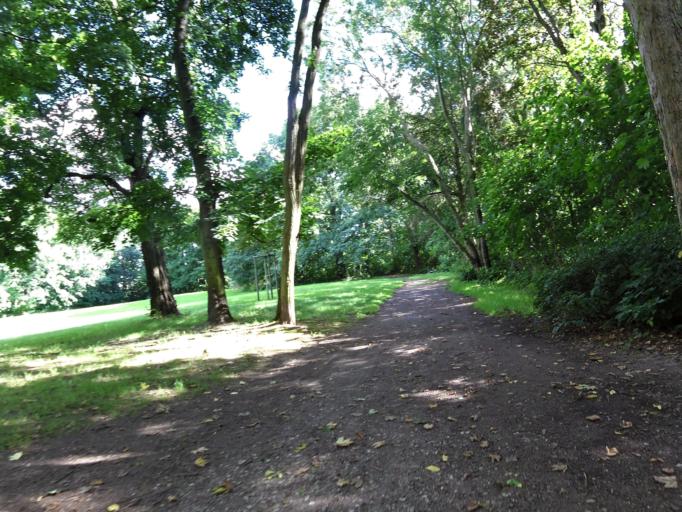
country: DE
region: Saxony
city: Markkleeberg
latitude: 51.2879
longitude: 12.4206
